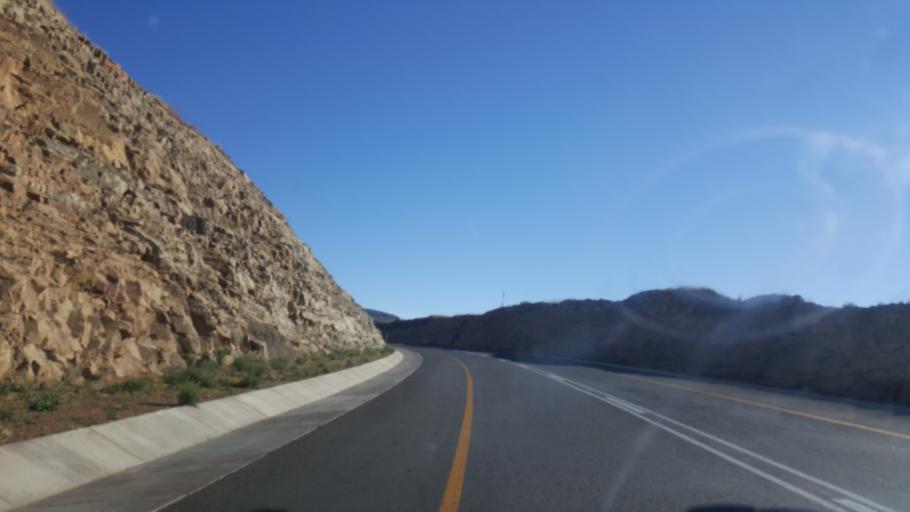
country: ZA
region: Eastern Cape
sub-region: Chris Hani District Municipality
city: Middelburg
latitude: -31.3800
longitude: 25.0342
